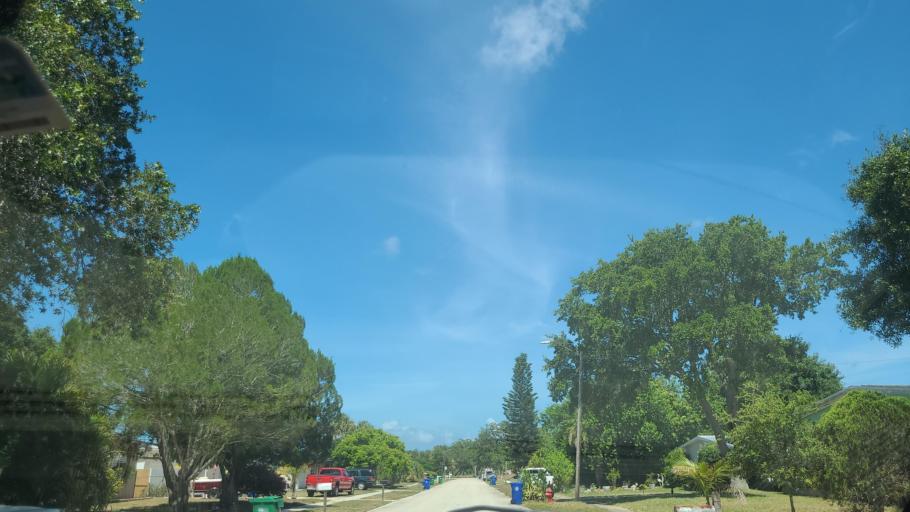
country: US
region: Florida
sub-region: Indian River County
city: Sebastian
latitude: 27.7886
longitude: -80.4608
